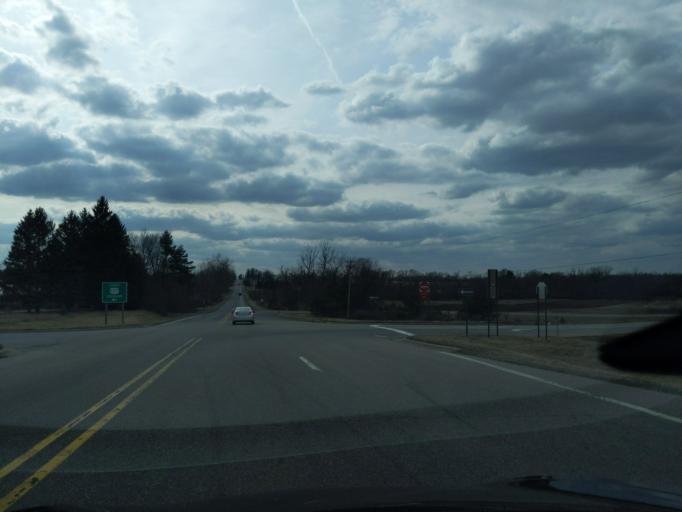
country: US
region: Michigan
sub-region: Ingham County
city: Mason
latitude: 42.5241
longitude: -84.4455
